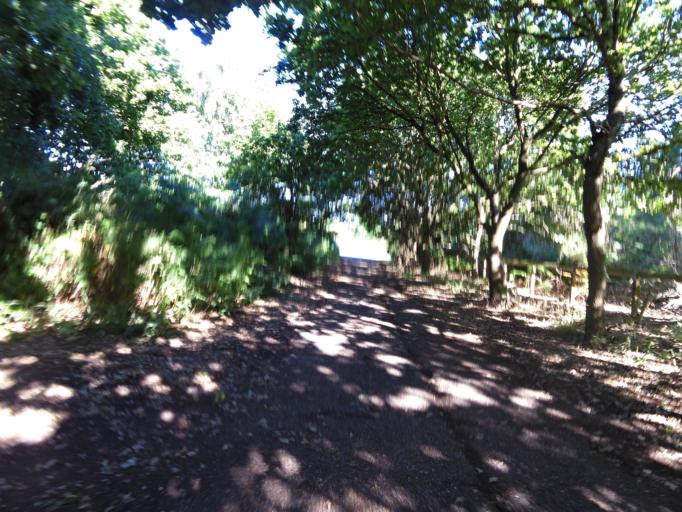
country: GB
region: England
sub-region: Suffolk
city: Kesgrave
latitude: 52.0675
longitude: 1.2723
